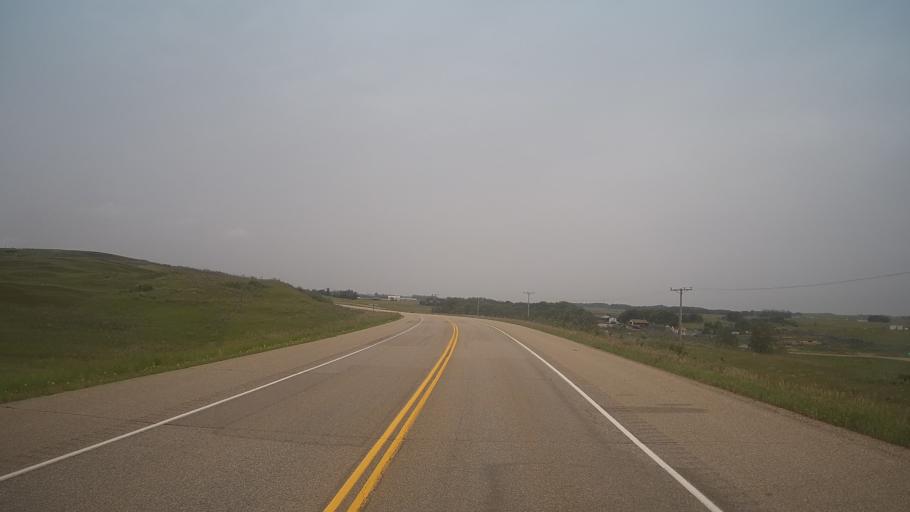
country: CA
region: Saskatchewan
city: Biggar
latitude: 52.0584
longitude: -107.8885
